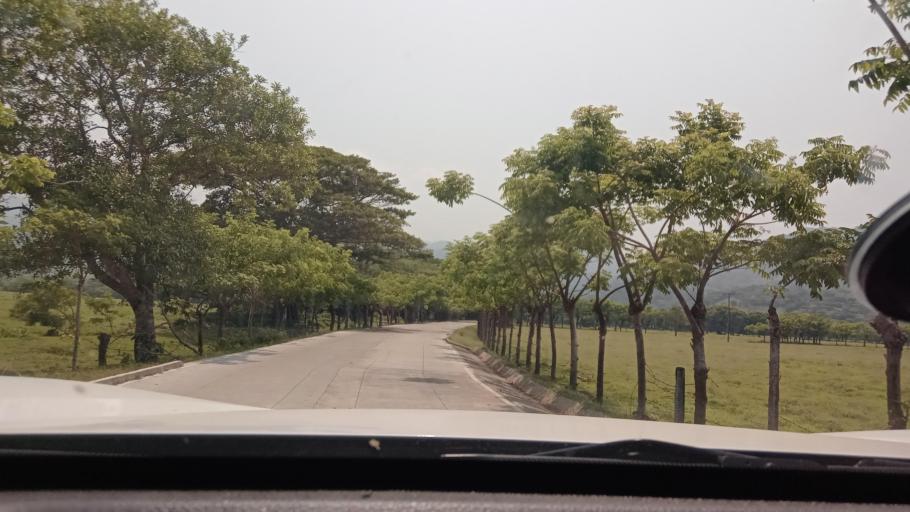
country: MX
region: Veracruz
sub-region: San Andres Tuxtla
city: Santa Rosa Abata
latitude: 18.5626
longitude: -95.0541
